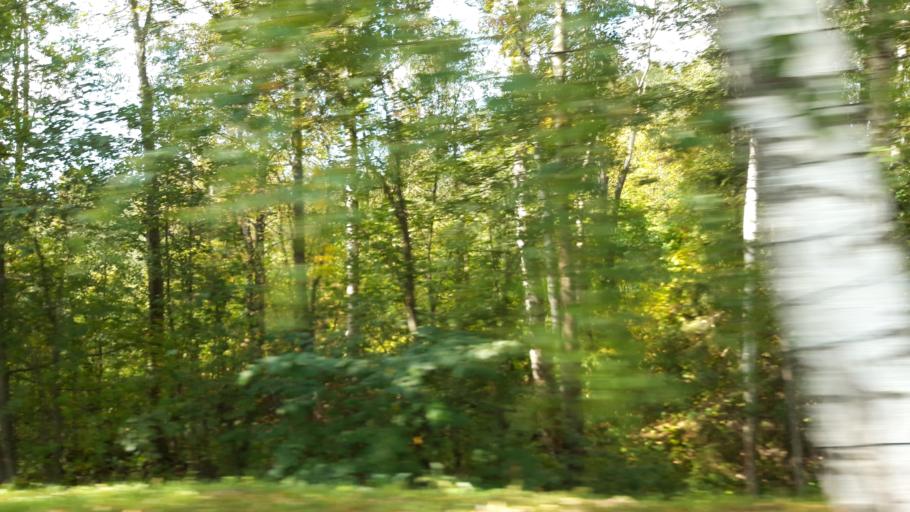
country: RU
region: Moskovskaya
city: Mendeleyevo
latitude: 56.0483
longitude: 37.2169
